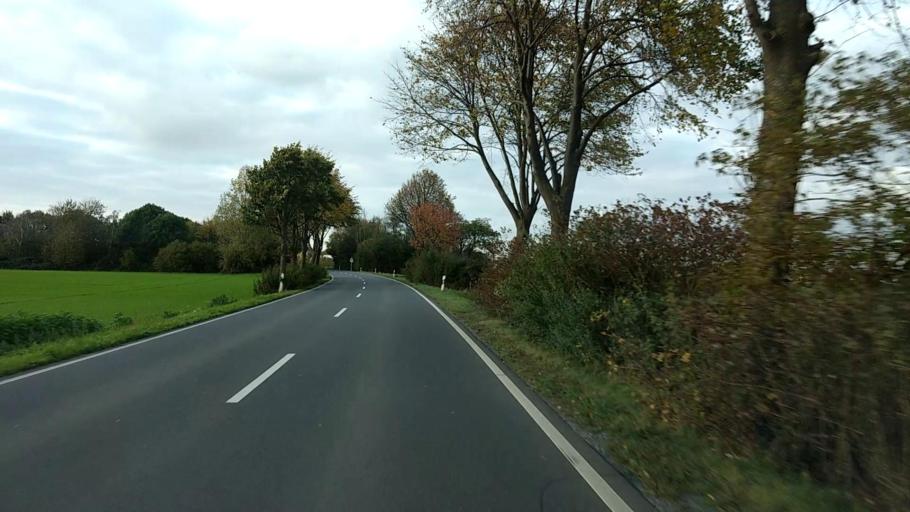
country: DE
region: North Rhine-Westphalia
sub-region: Regierungsbezirk Koln
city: Bergheim
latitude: 50.9056
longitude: 6.6400
